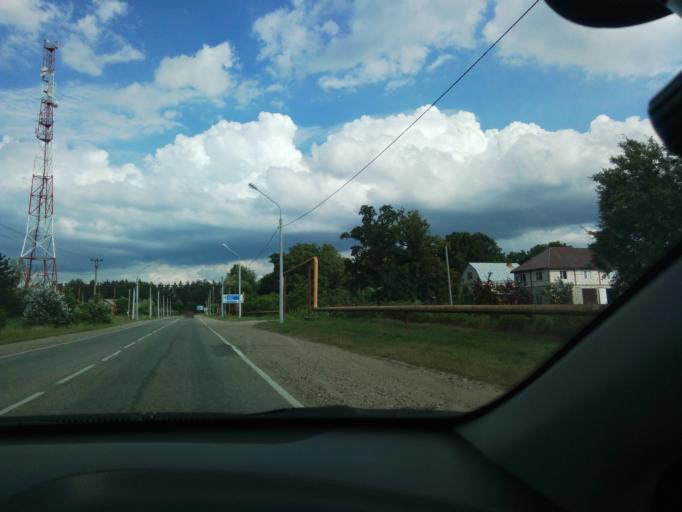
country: RU
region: Krasnodarskiy
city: Apsheronsk
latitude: 44.4377
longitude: 39.7600
